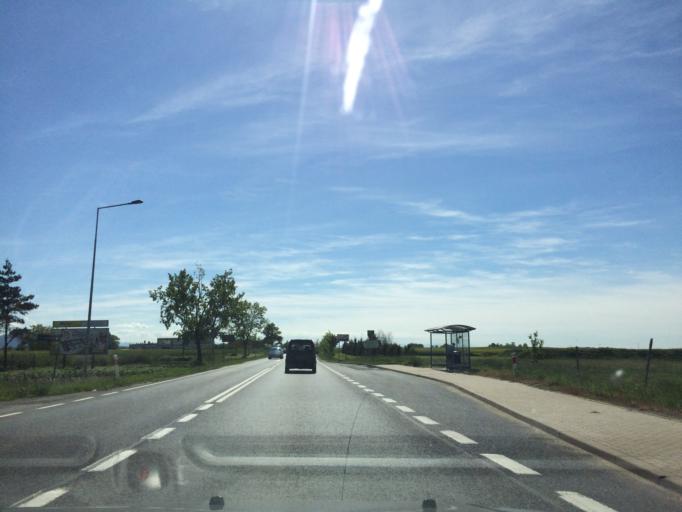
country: PL
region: Lower Silesian Voivodeship
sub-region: Powiat wroclawski
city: Gniechowice
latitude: 51.0120
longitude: 16.8701
